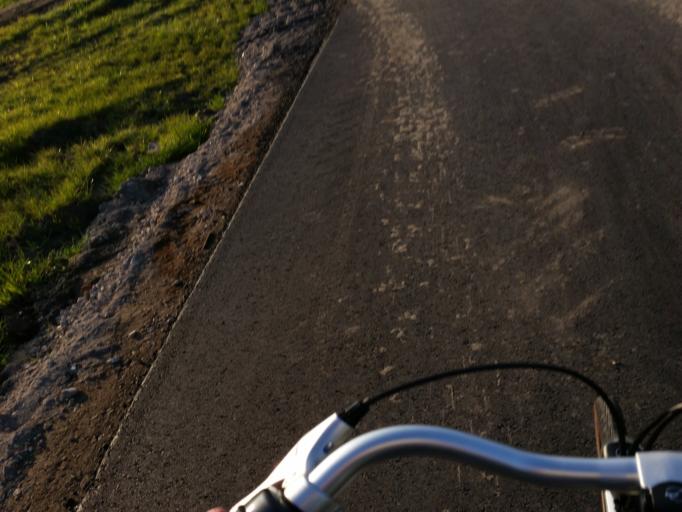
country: NL
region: South Holland
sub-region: Gemeente Lansingerland
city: Berkel en Rodenrijs
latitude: 52.0157
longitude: 4.4753
